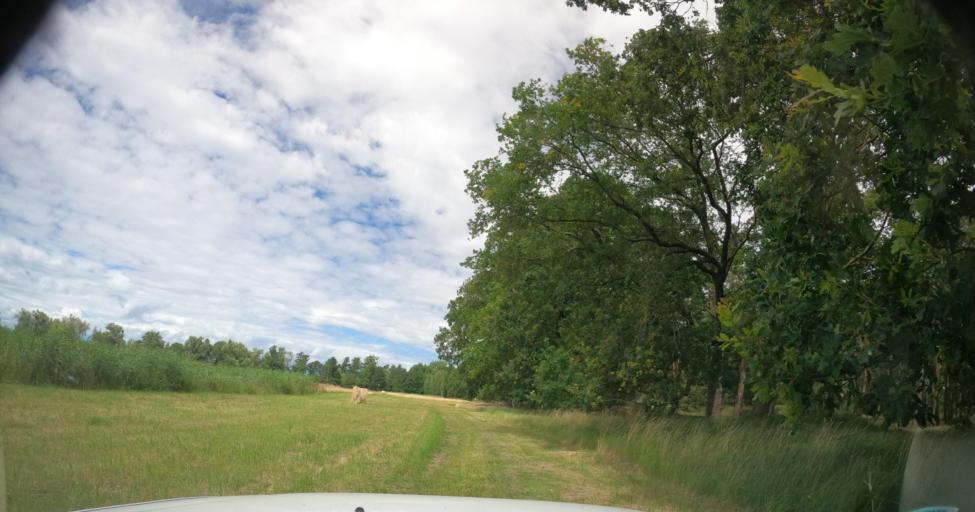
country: PL
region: West Pomeranian Voivodeship
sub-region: Powiat goleniowski
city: Stepnica
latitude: 53.7073
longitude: 14.5458
